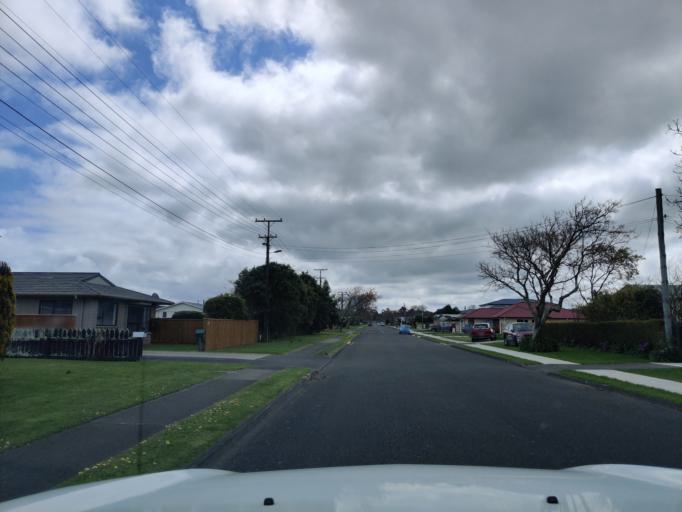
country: NZ
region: Manawatu-Wanganui
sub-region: Wanganui District
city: Wanganui
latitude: -39.9270
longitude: 175.0268
